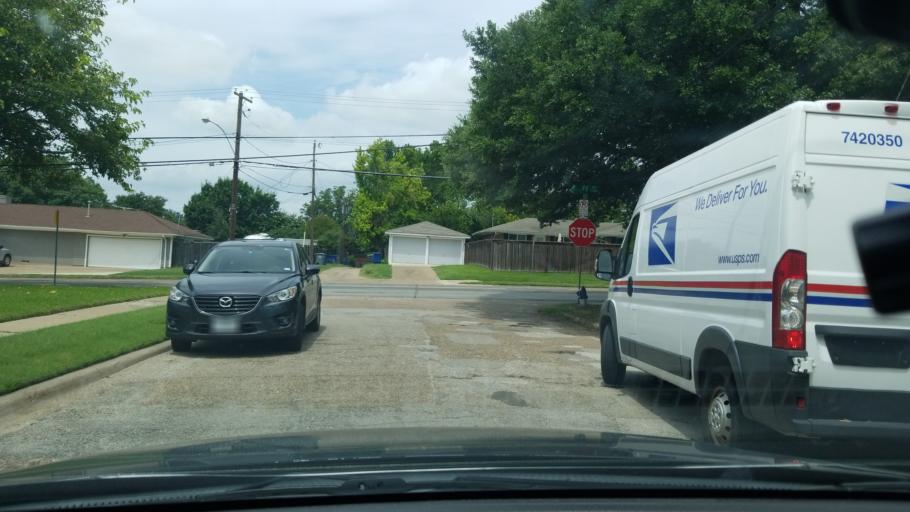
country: US
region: Texas
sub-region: Dallas County
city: Garland
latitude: 32.8247
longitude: -96.6836
